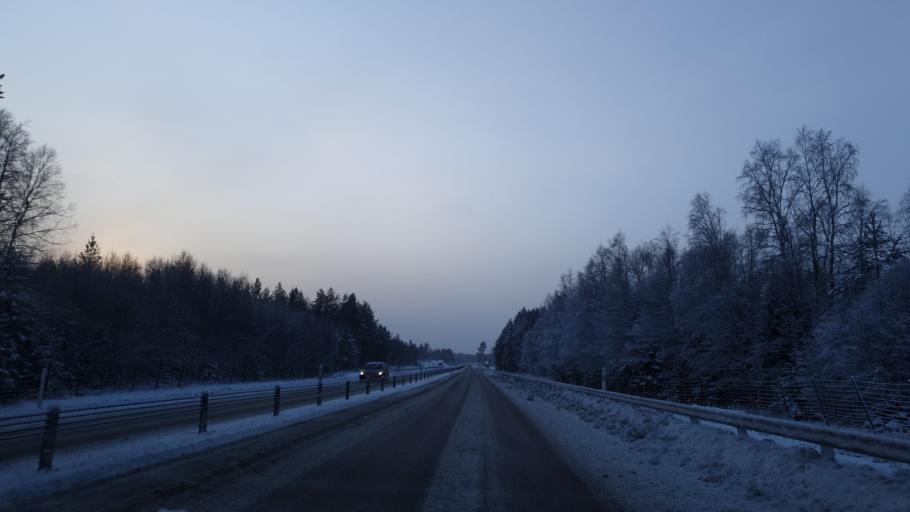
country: SE
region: Vaesterbotten
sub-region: Umea Kommun
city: Saevar
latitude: 63.9154
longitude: 20.5963
